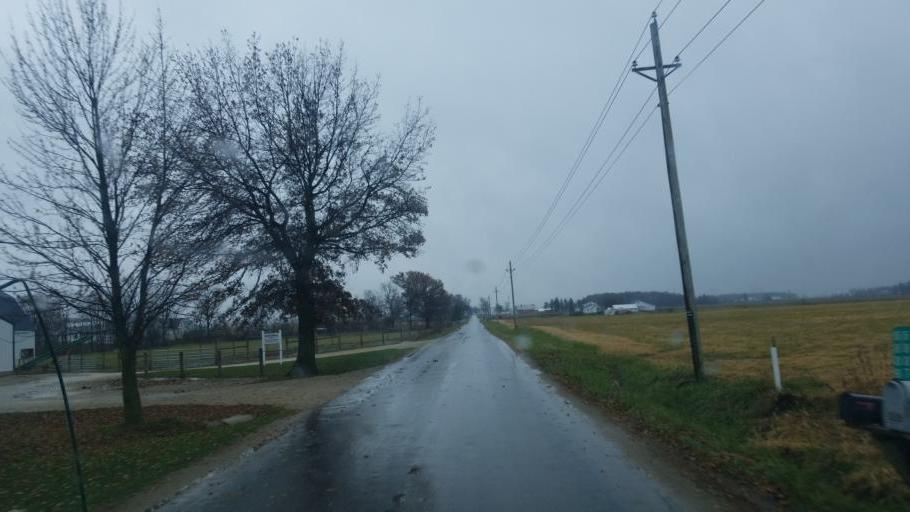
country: US
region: Indiana
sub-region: Adams County
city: Berne
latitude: 40.6482
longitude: -84.8785
